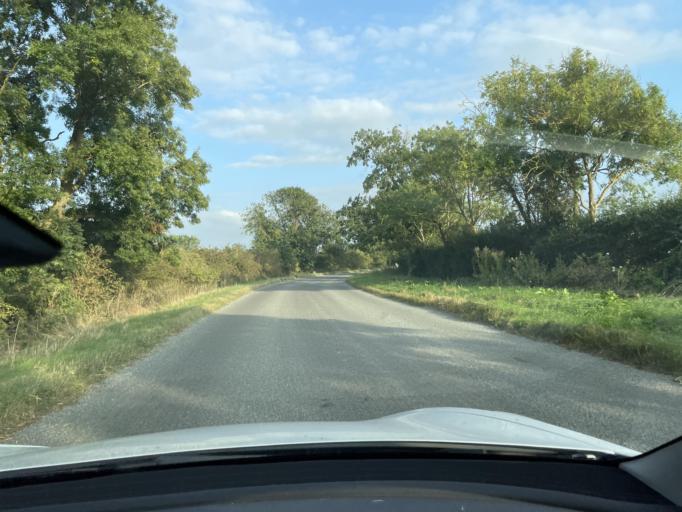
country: GB
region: England
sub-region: Bedford
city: Pertenhall
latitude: 52.3653
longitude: -0.4201
